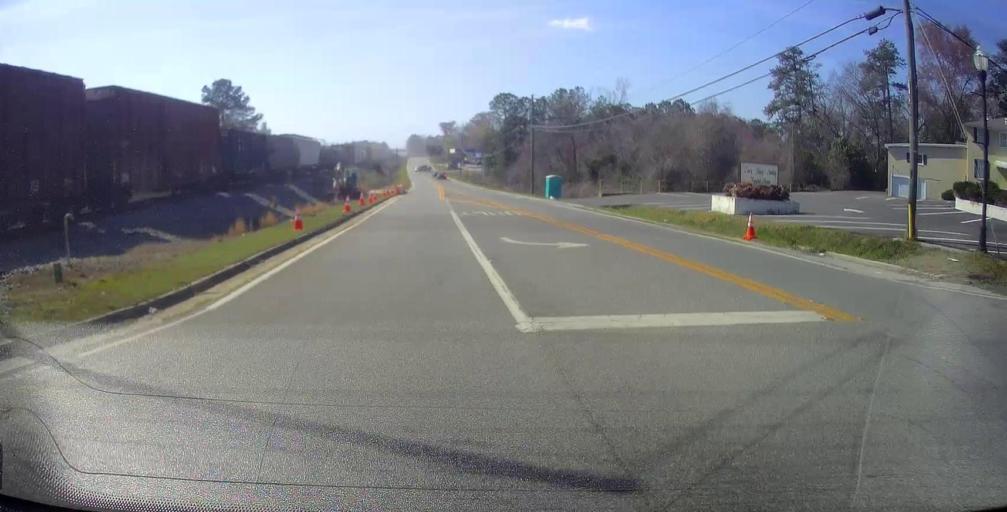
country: US
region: Georgia
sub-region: Wilkinson County
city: Gordon
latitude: 32.8823
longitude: -83.3359
